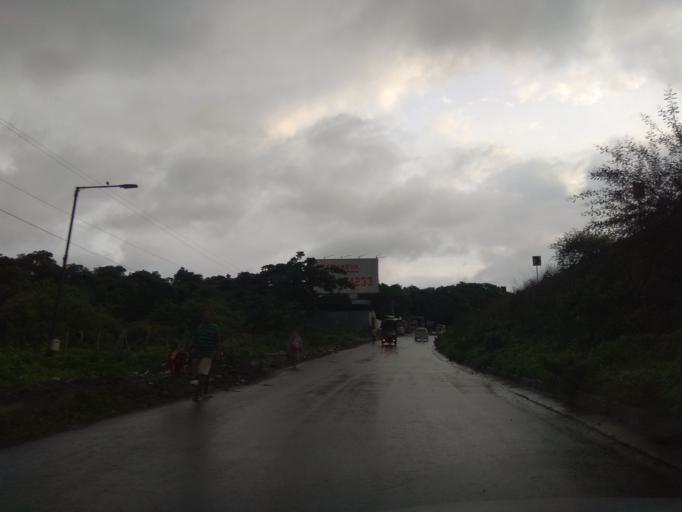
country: IN
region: Maharashtra
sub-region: Pune Division
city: Kharakvasla
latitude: 18.4949
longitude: 73.7876
